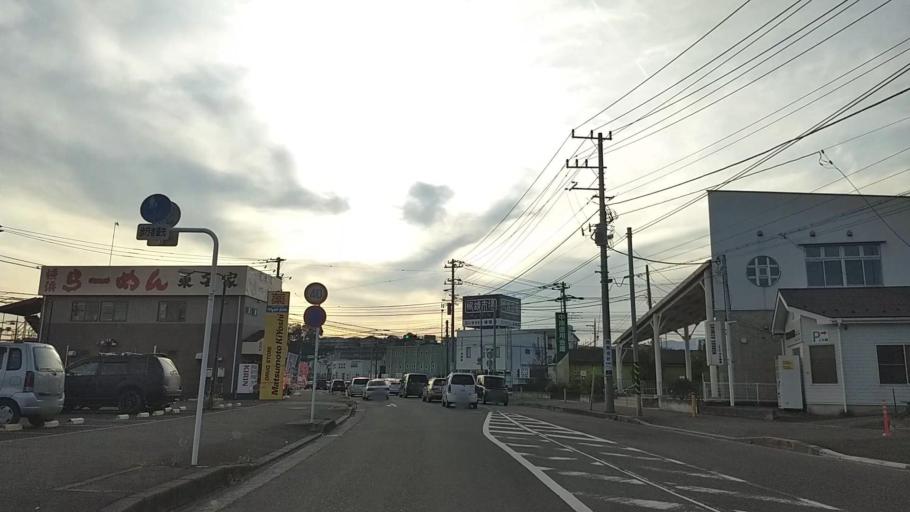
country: JP
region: Kanagawa
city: Atsugi
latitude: 35.4569
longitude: 139.3523
